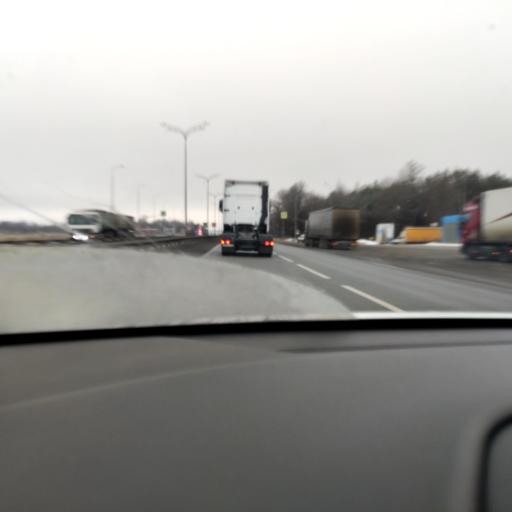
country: RU
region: Tatarstan
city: Osinovo
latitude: 55.7549
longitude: 48.8069
